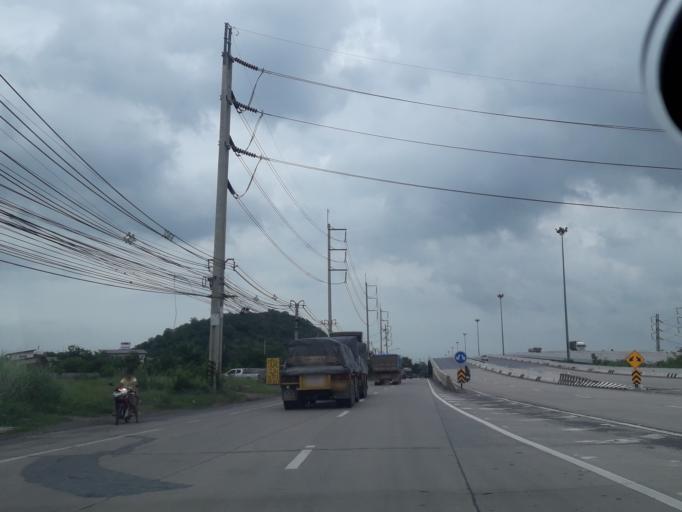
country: TH
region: Sara Buri
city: Saraburi
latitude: 14.5438
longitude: 100.9508
